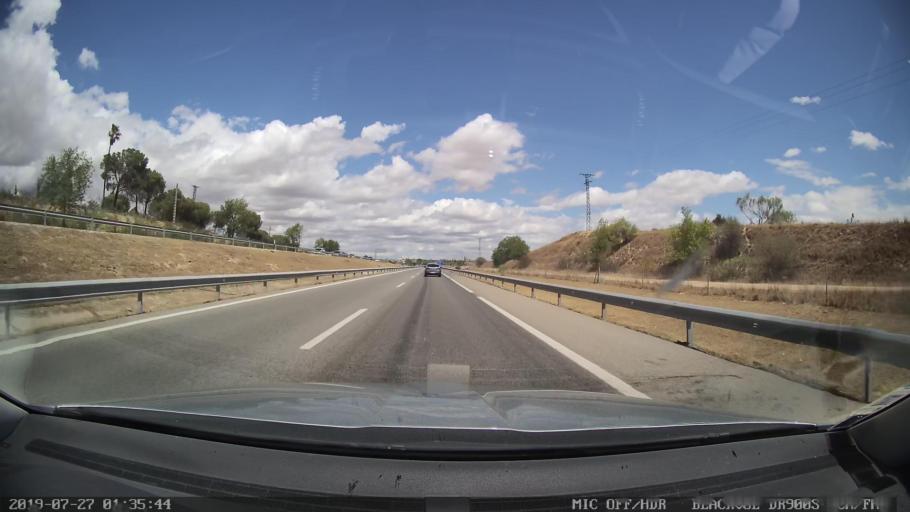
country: ES
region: Madrid
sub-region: Provincia de Madrid
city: Navalcarnero
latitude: 40.2696
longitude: -4.0354
